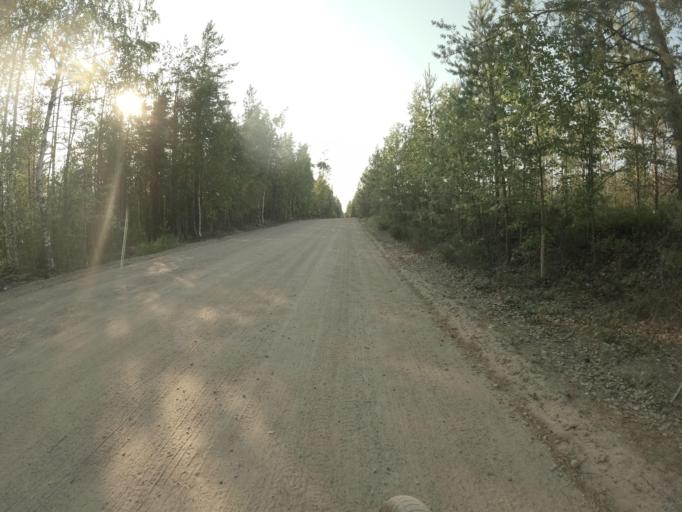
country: RU
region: Leningrad
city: Veshchevo
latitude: 60.4565
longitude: 29.2496
